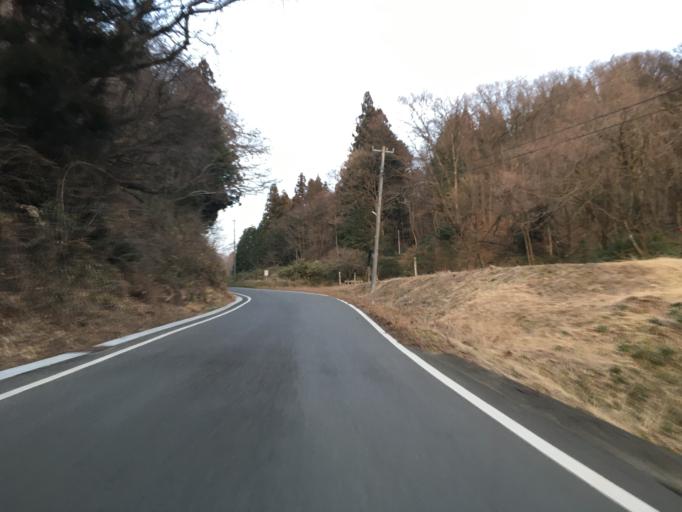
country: JP
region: Fukushima
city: Ishikawa
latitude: 37.0764
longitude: 140.3088
